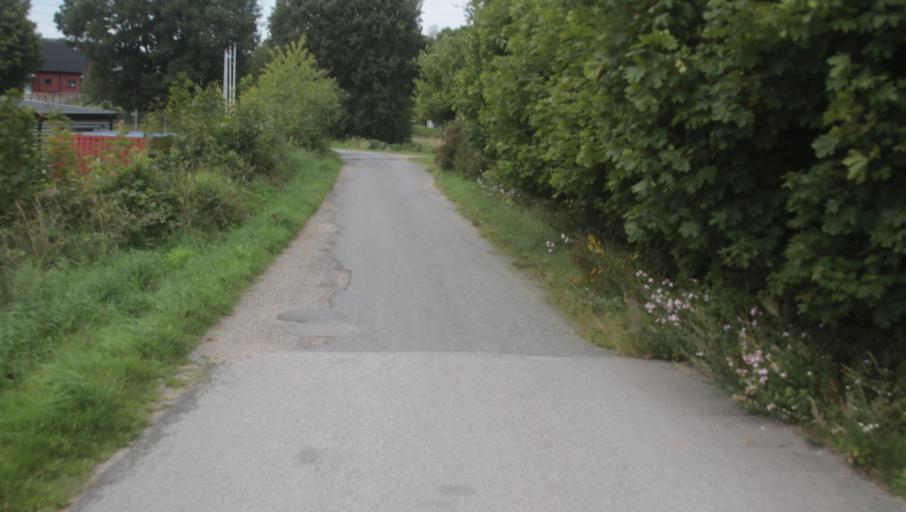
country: SE
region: Blekinge
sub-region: Karlshamns Kommun
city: Karlshamn
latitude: 56.2215
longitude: 14.8338
